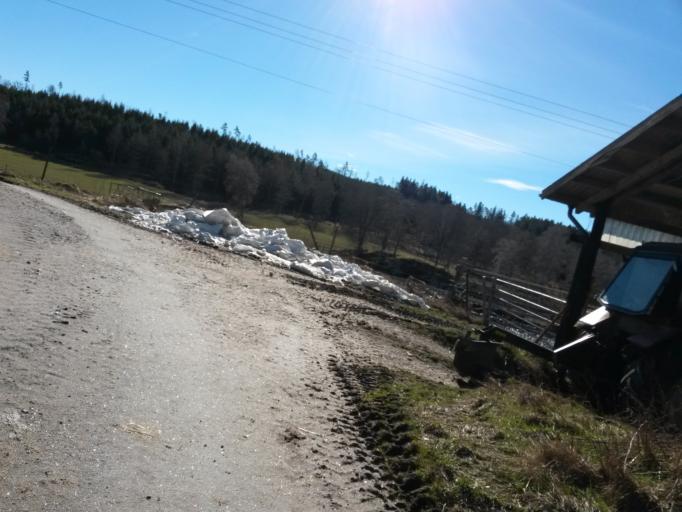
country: SE
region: Vaestra Goetaland
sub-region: Vargarda Kommun
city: Jonstorp
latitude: 57.9710
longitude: 12.6698
